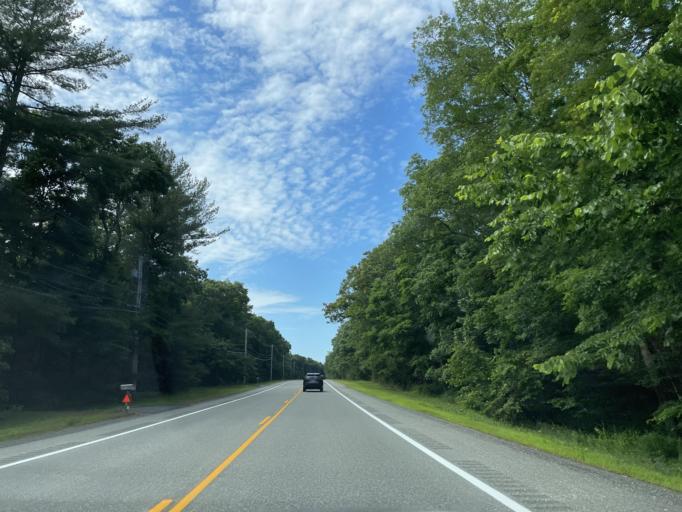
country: US
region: Rhode Island
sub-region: Kent County
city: West Greenwich
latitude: 41.6527
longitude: -71.6938
